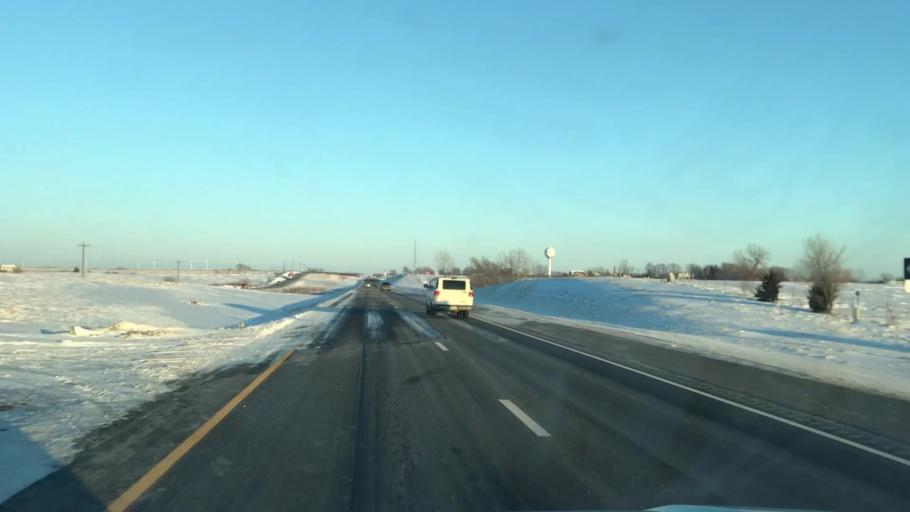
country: US
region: Missouri
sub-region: Clinton County
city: Gower
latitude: 39.7620
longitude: -94.5173
